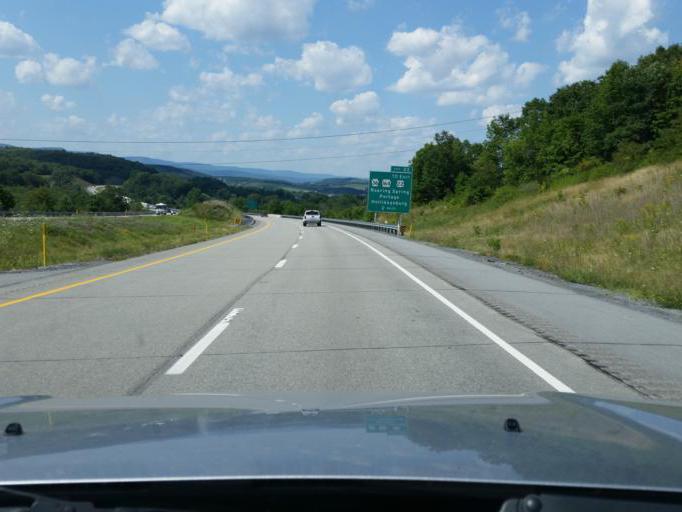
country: US
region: Pennsylvania
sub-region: Blair County
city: Roaring Spring
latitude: 40.3361
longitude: -78.4293
